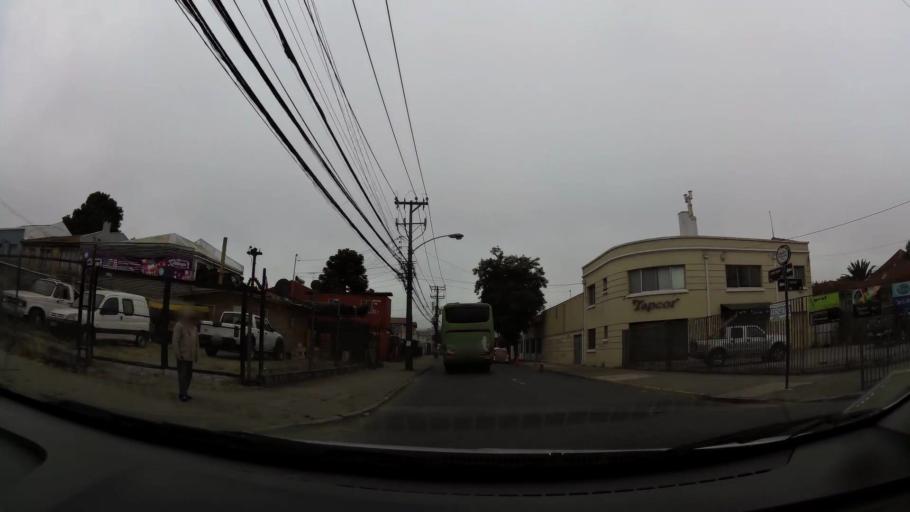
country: CL
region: Biobio
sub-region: Provincia de Concepcion
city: Concepcion
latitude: -36.8197
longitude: -73.0525
